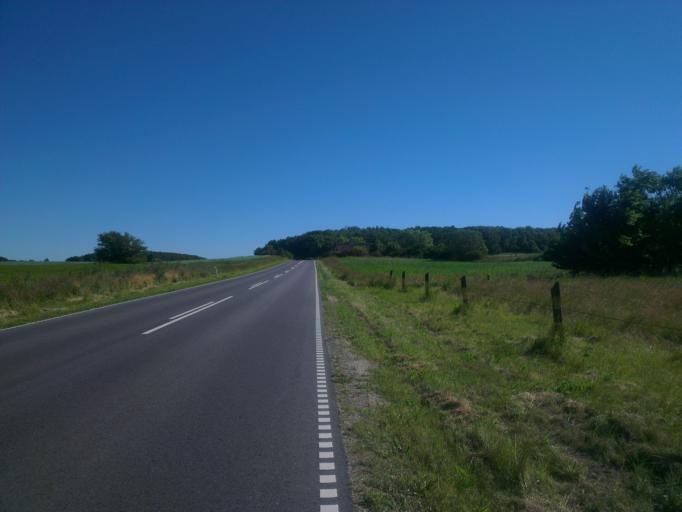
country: DK
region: Capital Region
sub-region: Frederikssund Kommune
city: Jaegerspris
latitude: 55.8804
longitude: 11.9547
